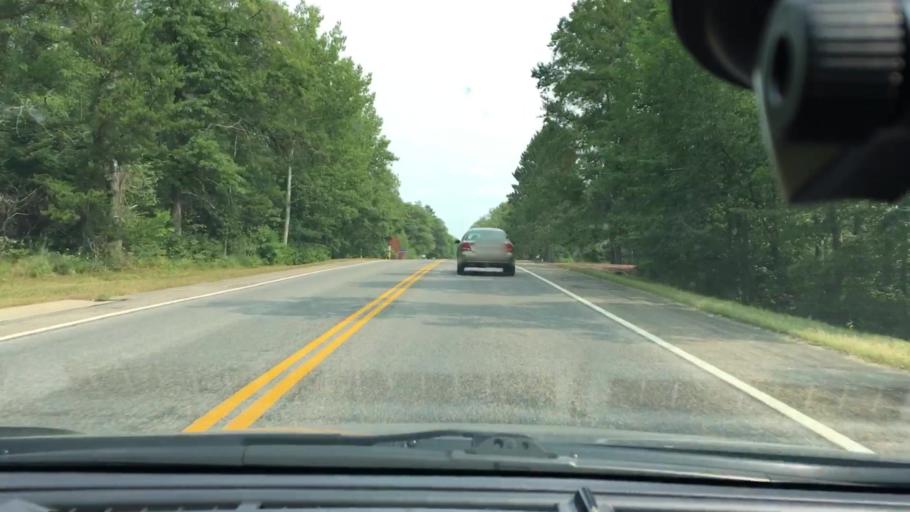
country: US
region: Minnesota
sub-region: Cass County
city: East Gull Lake
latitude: 46.4128
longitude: -94.3153
